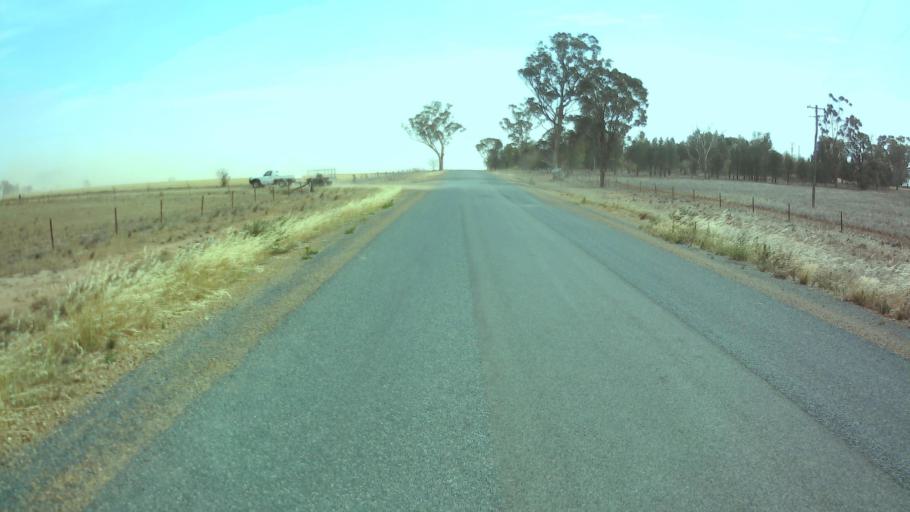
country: AU
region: New South Wales
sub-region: Weddin
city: Grenfell
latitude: -33.7483
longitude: 147.9912
